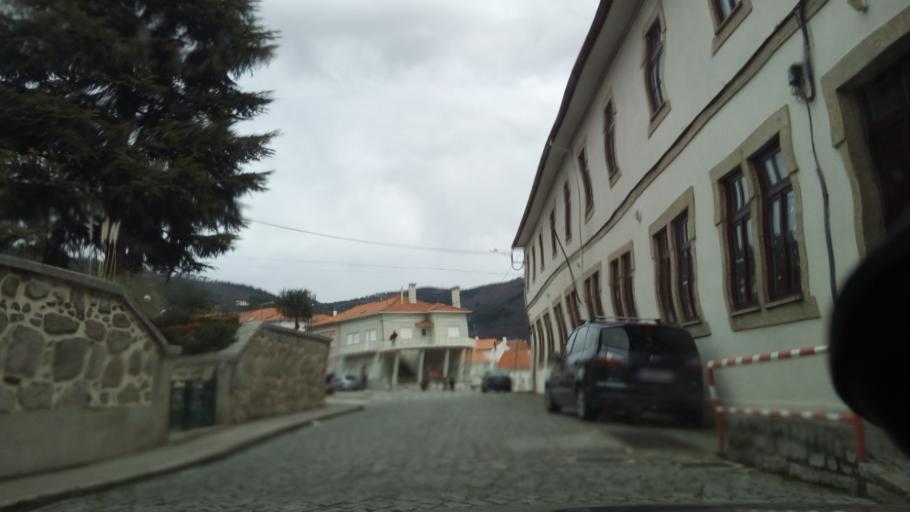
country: PT
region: Guarda
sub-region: Manteigas
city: Manteigas
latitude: 40.4009
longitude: -7.5409
